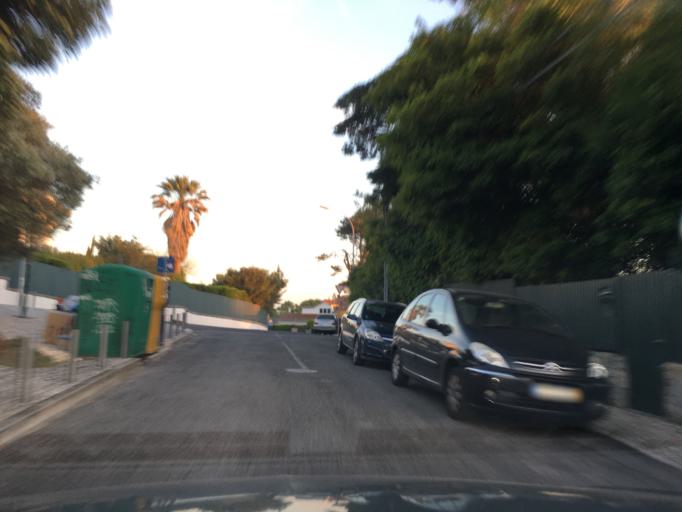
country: PT
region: Lisbon
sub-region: Oeiras
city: Paco de Arcos
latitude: 38.7005
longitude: -9.2894
